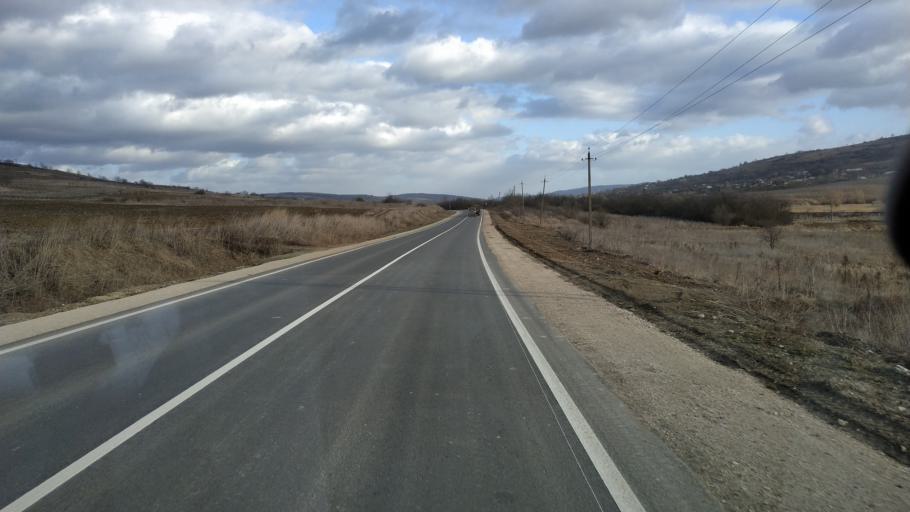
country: MD
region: Calarasi
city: Calarasi
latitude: 47.2941
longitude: 28.1700
